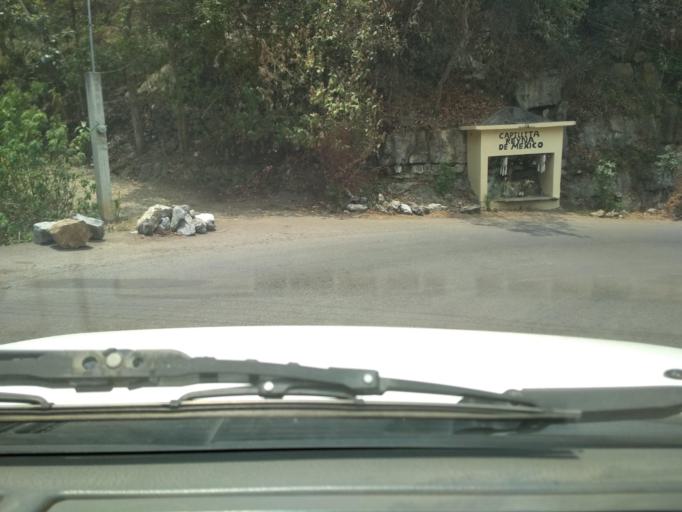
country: MX
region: Veracruz
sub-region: Camerino Z. Mendoza
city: La Cuesta
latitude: 18.7950
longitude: -97.1736
